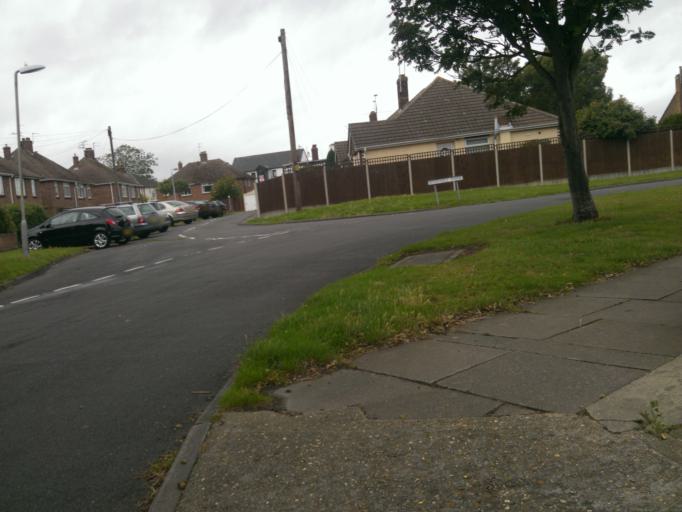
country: GB
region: England
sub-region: Essex
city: Clacton-on-Sea
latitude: 51.8020
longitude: 1.1557
